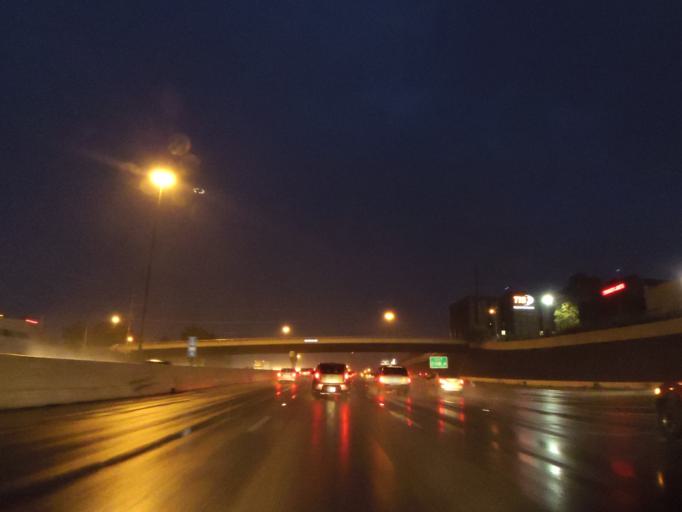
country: US
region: Tennessee
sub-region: Blount County
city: Louisville
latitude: 35.9277
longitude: -84.0471
